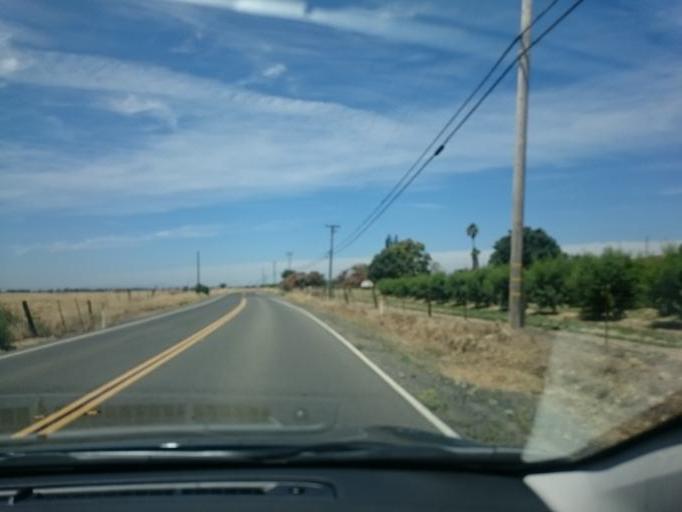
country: US
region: California
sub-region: Stanislaus County
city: Waterford
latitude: 37.6466
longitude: -120.6810
